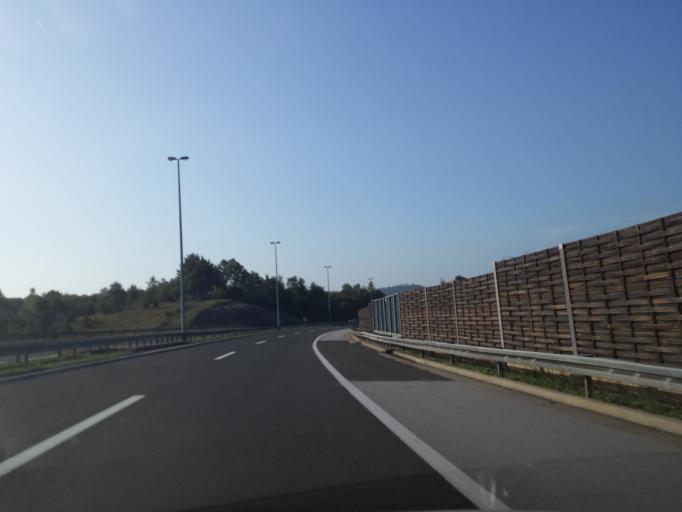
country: HR
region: Karlovacka
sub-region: Grad Ogulin
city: Ogulin
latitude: 45.4006
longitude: 15.2508
